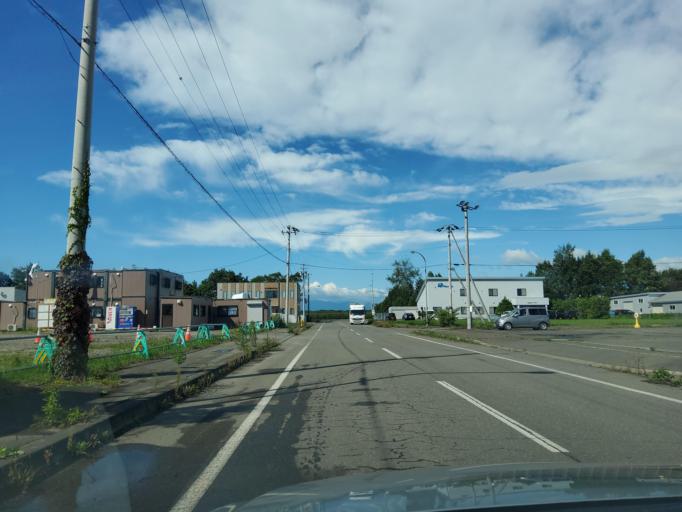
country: JP
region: Hokkaido
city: Otofuke
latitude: 42.9821
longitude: 143.1785
